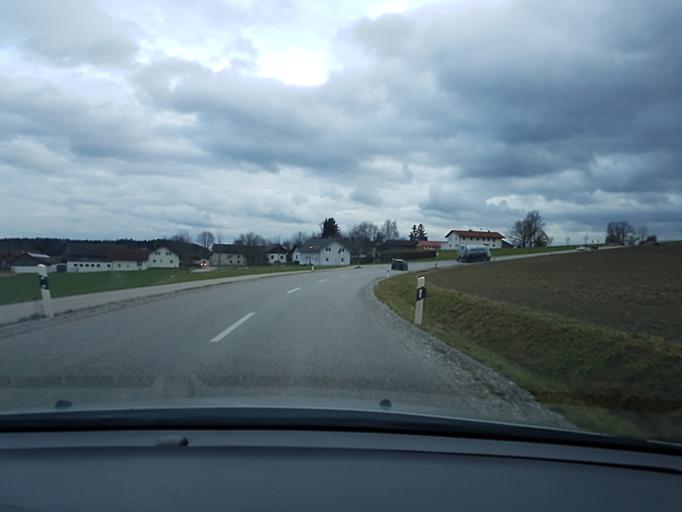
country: DE
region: Bavaria
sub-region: Lower Bavaria
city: Furth
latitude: 48.4145
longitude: 12.3709
